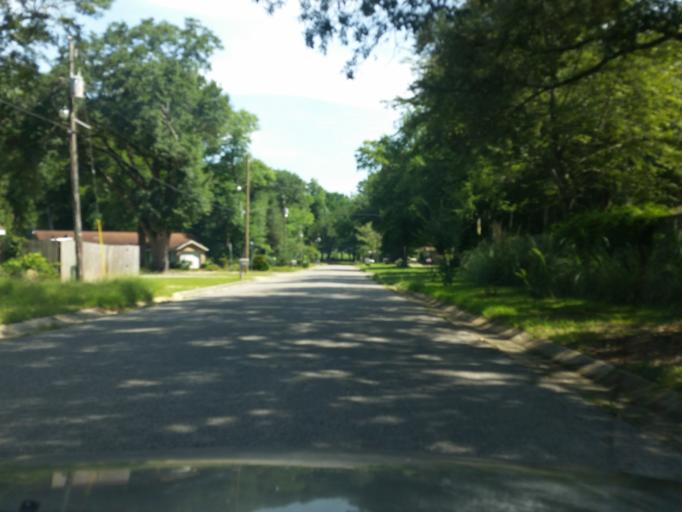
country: US
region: Florida
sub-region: Escambia County
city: Ferry Pass
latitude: 30.5146
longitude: -87.1926
